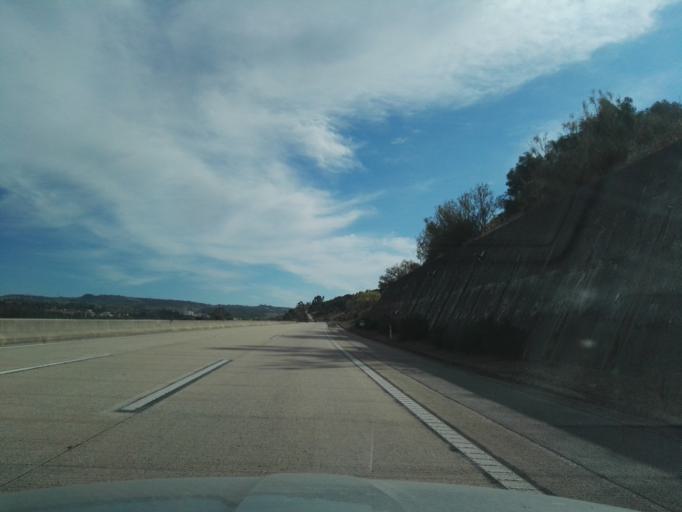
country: PT
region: Lisbon
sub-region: Loures
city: Bucelas
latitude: 38.8947
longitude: -9.1196
